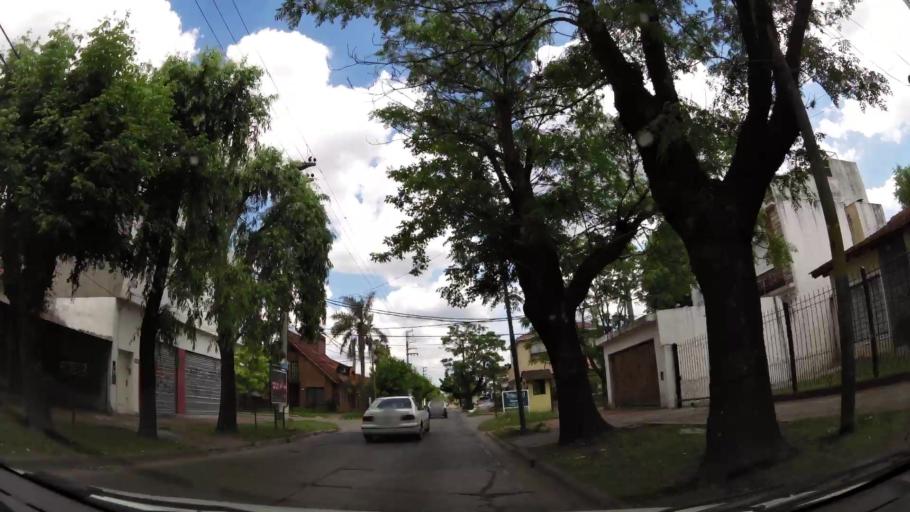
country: AR
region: Buenos Aires
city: Ituzaingo
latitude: -34.6547
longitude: -58.6747
